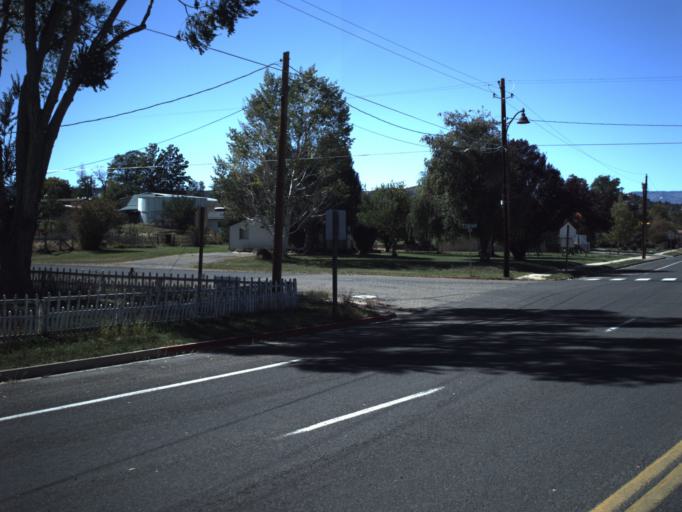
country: US
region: Utah
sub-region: Wayne County
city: Loa
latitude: 37.7702
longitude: -111.5960
